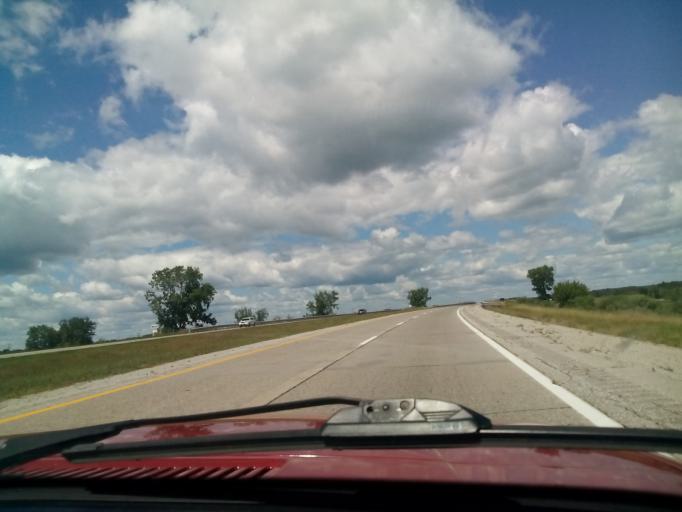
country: US
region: Michigan
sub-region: Bay County
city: Auburn
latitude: 43.6654
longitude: -84.0106
